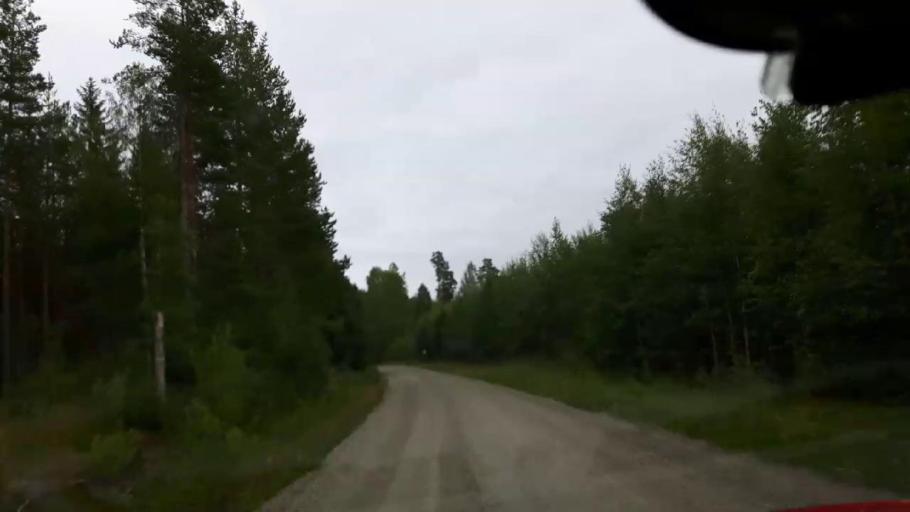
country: SE
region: Vaesternorrland
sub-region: Ange Kommun
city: Ange
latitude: 62.8037
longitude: 15.7518
